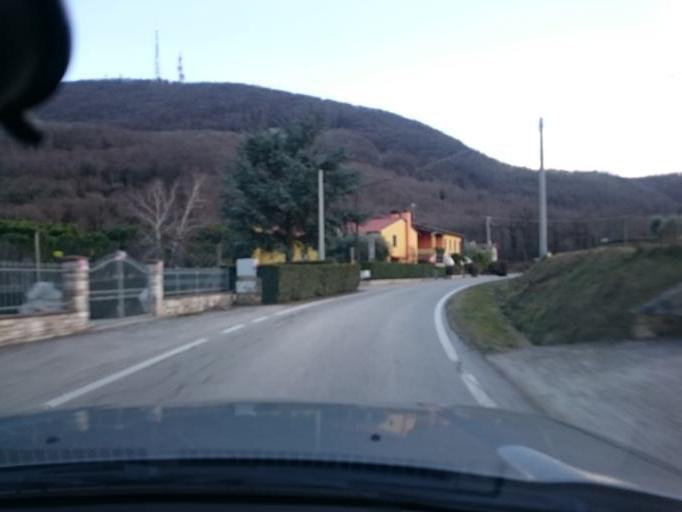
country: IT
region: Veneto
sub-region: Provincia di Padova
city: Fontanafredda
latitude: 45.3193
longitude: 11.6754
